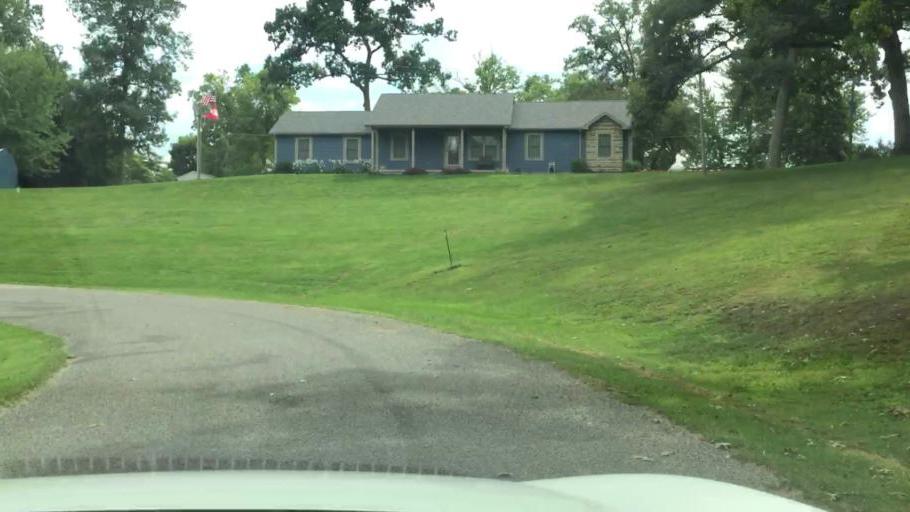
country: US
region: Ohio
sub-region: Champaign County
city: Urbana
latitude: 40.0970
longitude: -83.7049
